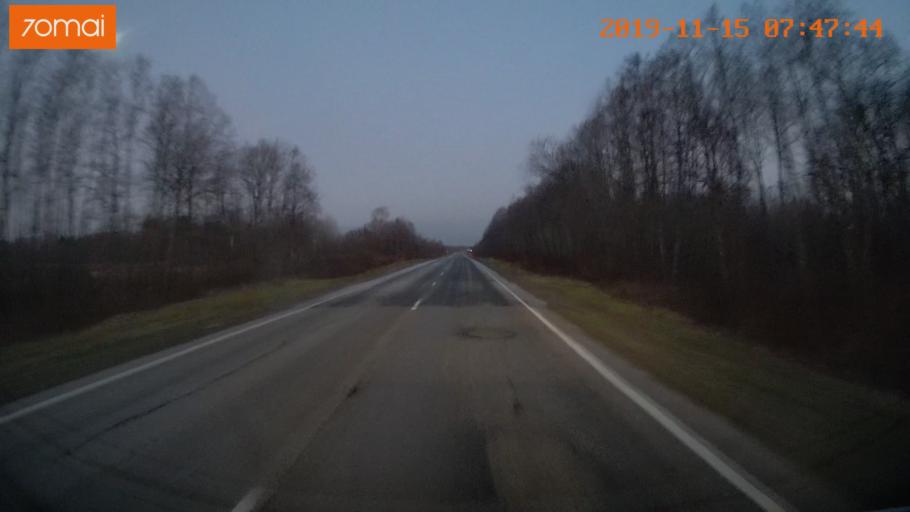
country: RU
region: Vologda
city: Sheksna
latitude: 58.8437
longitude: 38.2567
